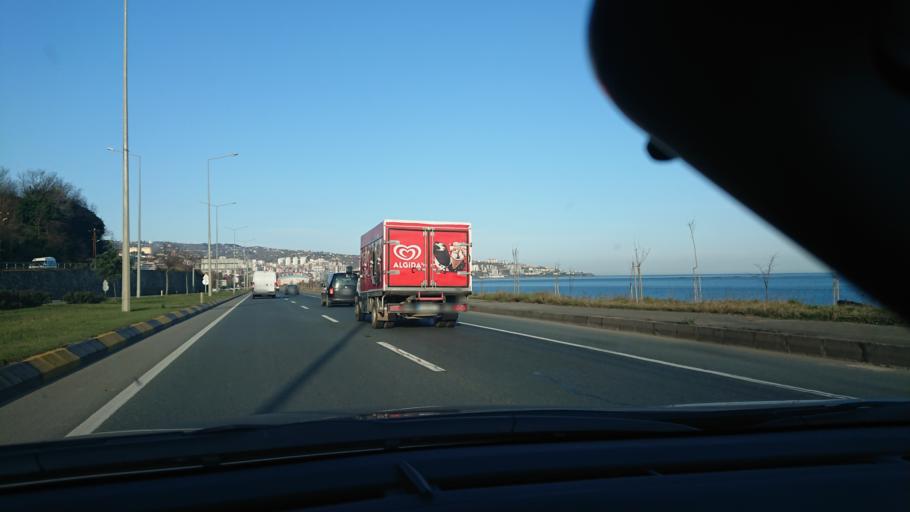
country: TR
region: Trabzon
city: Yomra
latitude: 40.9536
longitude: 39.8808
